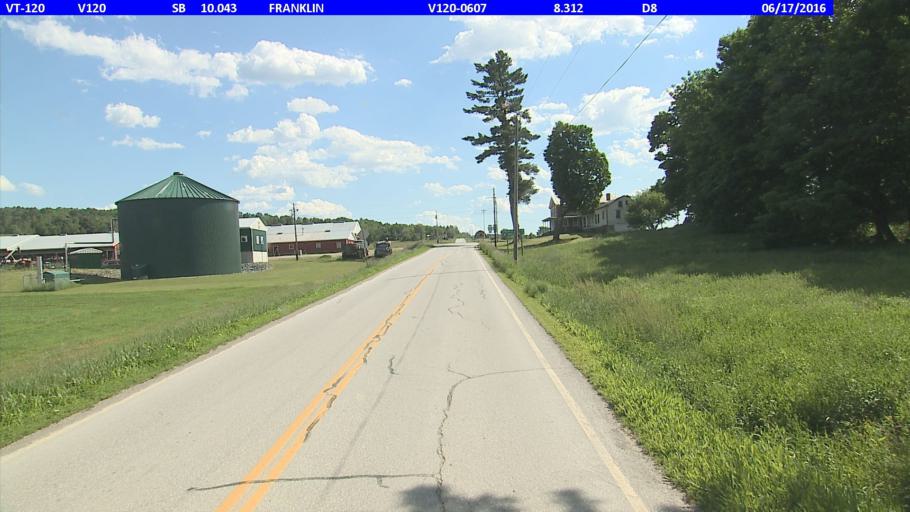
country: US
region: Vermont
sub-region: Franklin County
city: Enosburg Falls
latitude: 44.9953
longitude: -72.8322
